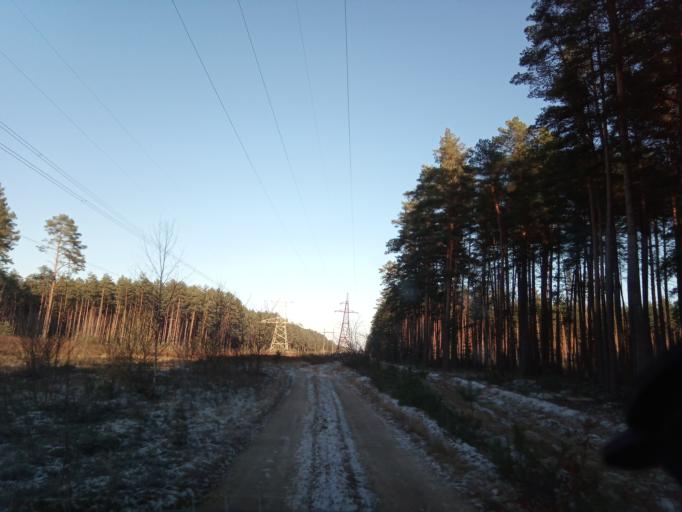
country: LT
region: Alytaus apskritis
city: Druskininkai
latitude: 53.9555
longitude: 23.8622
